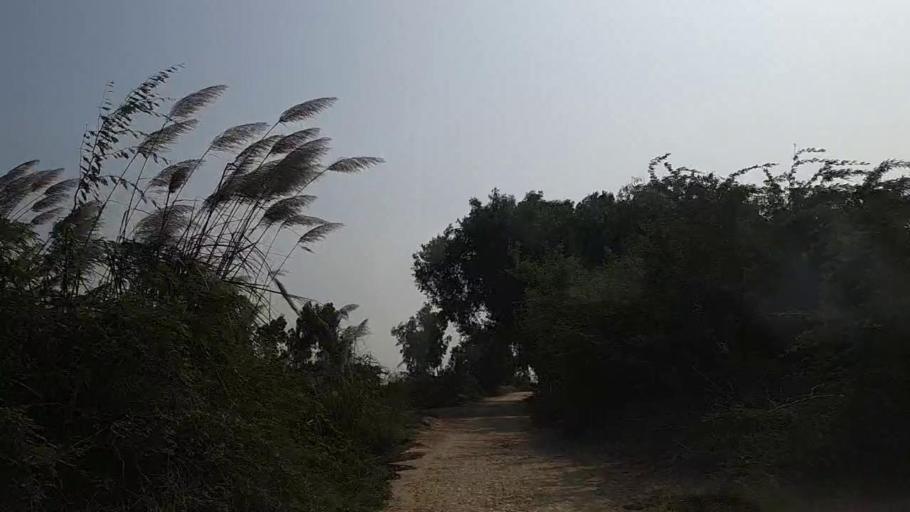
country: PK
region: Sindh
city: Mirpur Sakro
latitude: 24.5924
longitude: 67.7184
